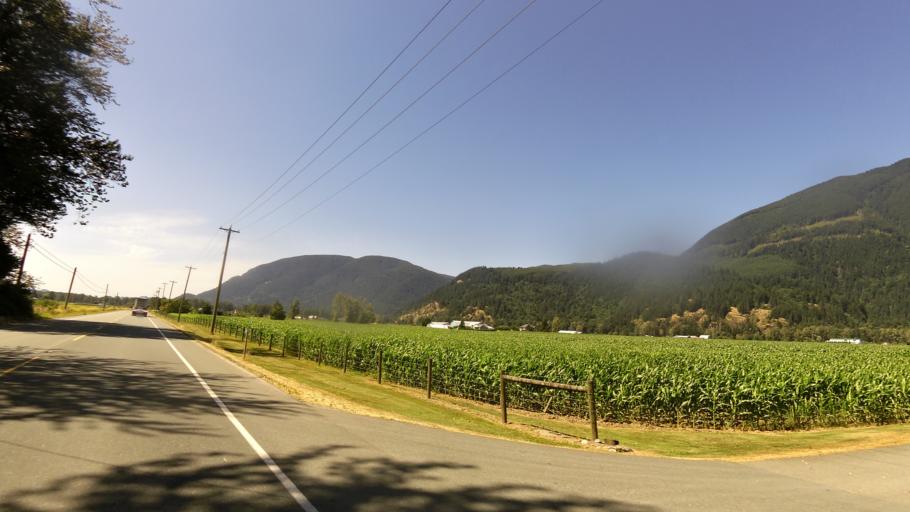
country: CA
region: British Columbia
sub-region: Fraser Valley Regional District
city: Chilliwack
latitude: 49.1693
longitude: -122.1128
